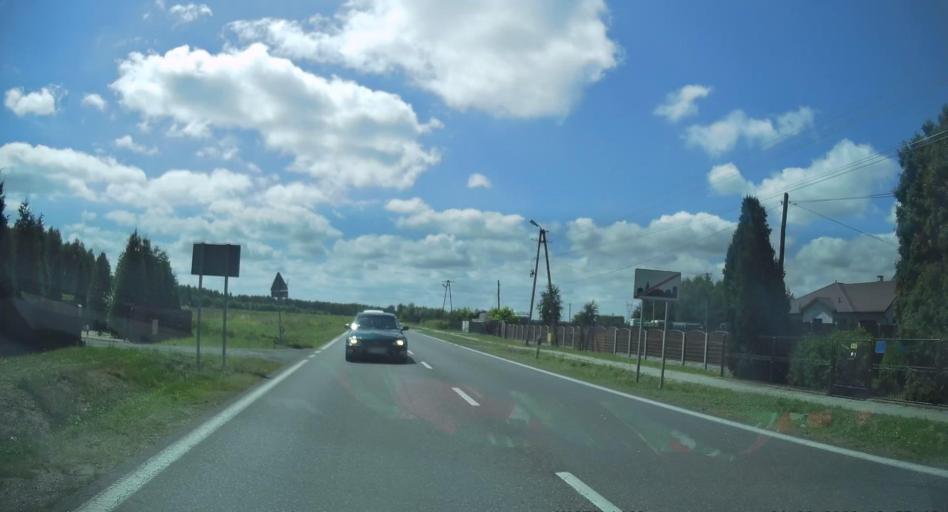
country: PL
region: Subcarpathian Voivodeship
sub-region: Powiat mielecki
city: Padew Narodowa
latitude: 50.4148
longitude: 21.4792
